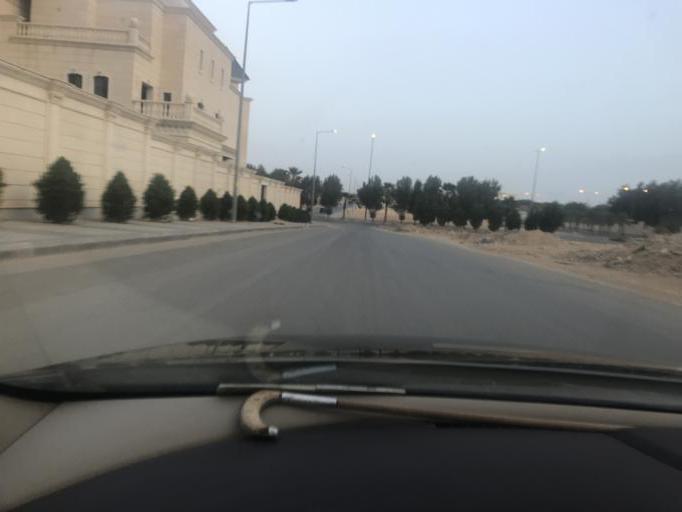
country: SA
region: Ar Riyad
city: Riyadh
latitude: 24.7259
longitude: 46.7495
